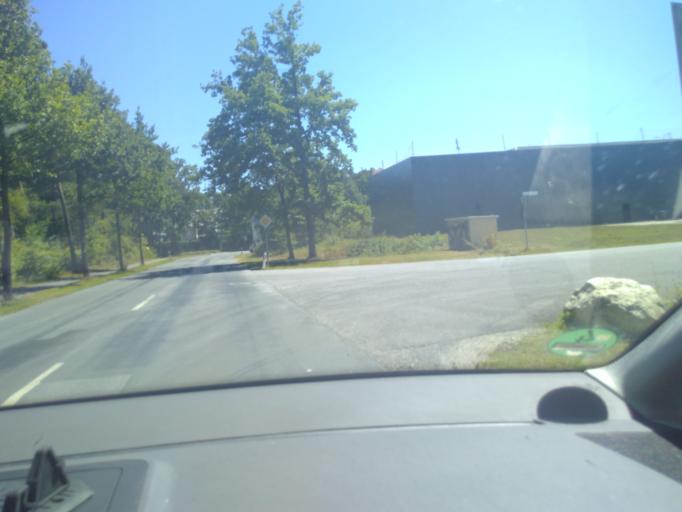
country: DE
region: North Rhine-Westphalia
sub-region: Regierungsbezirk Detmold
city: Verl
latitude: 51.8871
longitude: 8.4581
